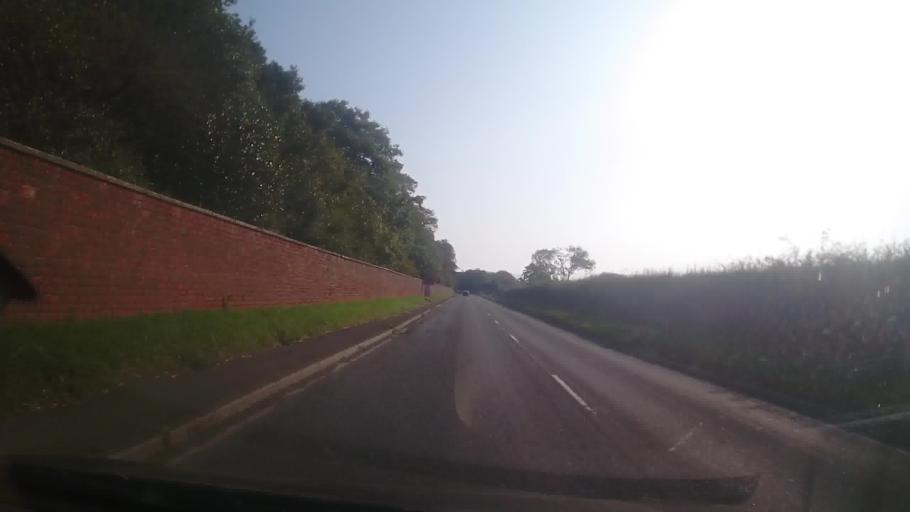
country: GB
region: England
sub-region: Shropshire
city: Berrington
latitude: 52.6799
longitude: -2.6701
